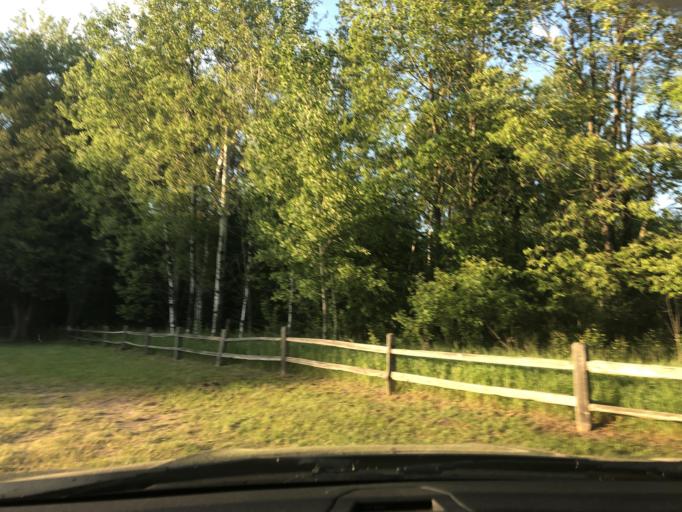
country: US
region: Michigan
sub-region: Missaukee County
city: Lake City
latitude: 44.4676
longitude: -85.1237
